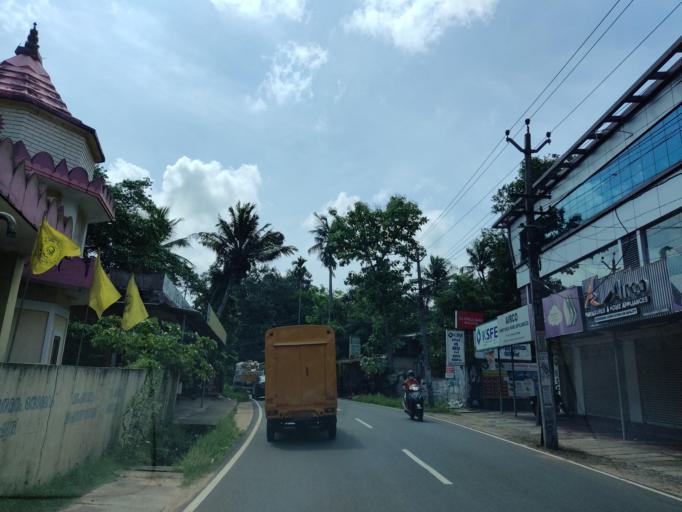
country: IN
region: Kerala
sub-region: Alappuzha
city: Mavelikara
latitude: 9.2775
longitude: 76.5364
